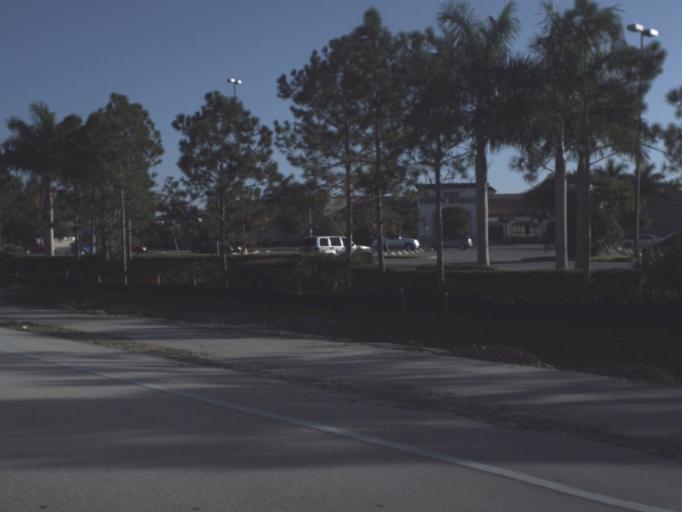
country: US
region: Florida
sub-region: Lee County
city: Villas
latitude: 26.5473
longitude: -81.8714
